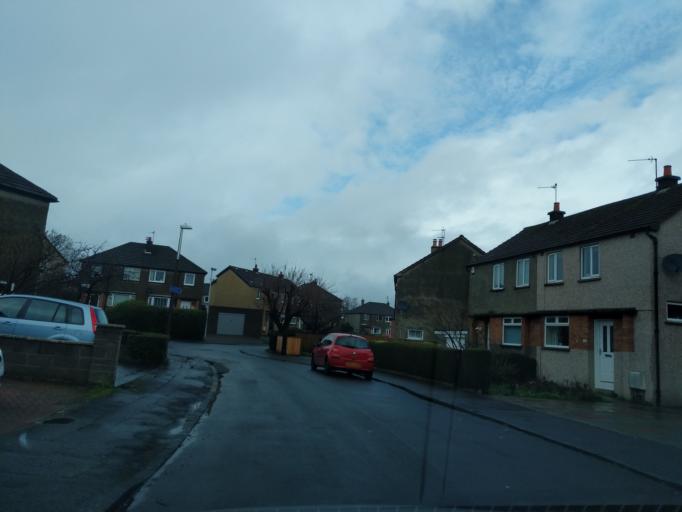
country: GB
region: Scotland
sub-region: Edinburgh
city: Colinton
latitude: 55.9375
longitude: -3.2865
